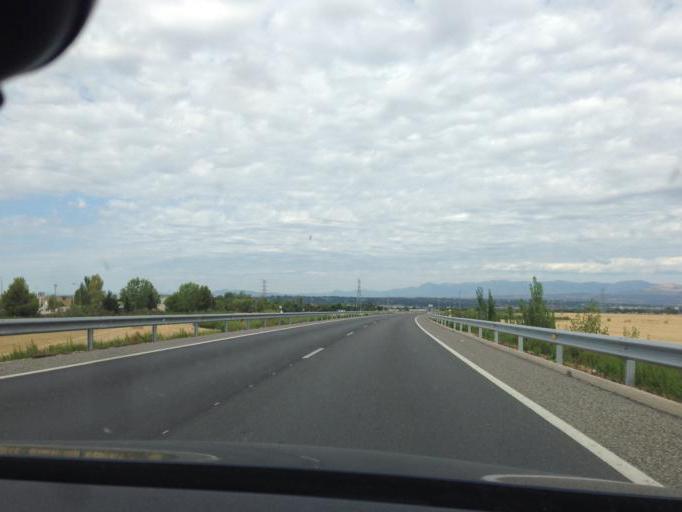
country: ES
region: Madrid
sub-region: Provincia de Madrid
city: Cobena
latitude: 40.5775
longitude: -3.5394
